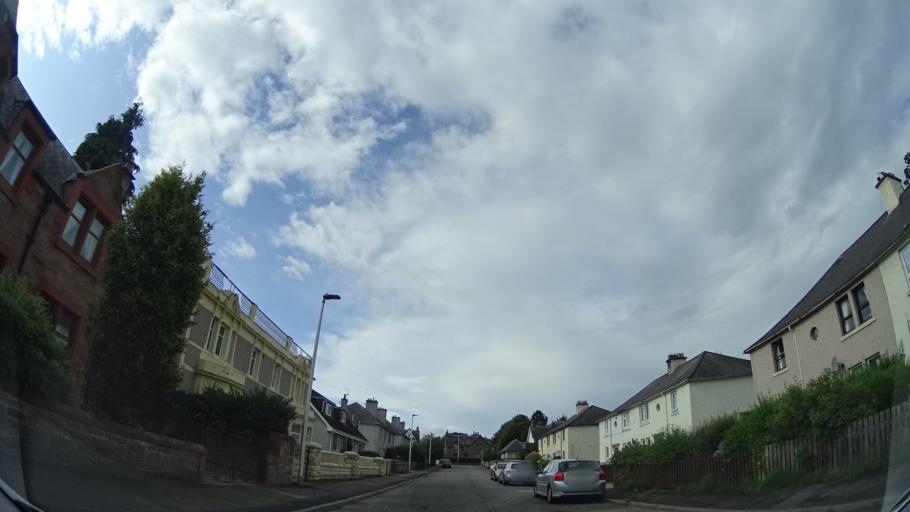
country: GB
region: Scotland
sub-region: Highland
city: Inverness
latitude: 57.4790
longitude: -4.2408
